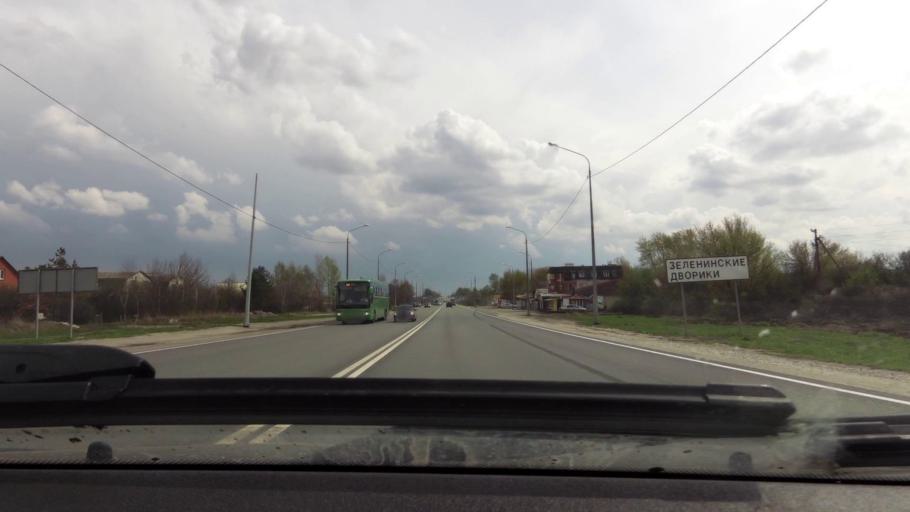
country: RU
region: Rjazan
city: Bagramovo
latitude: 54.7330
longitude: 39.4587
